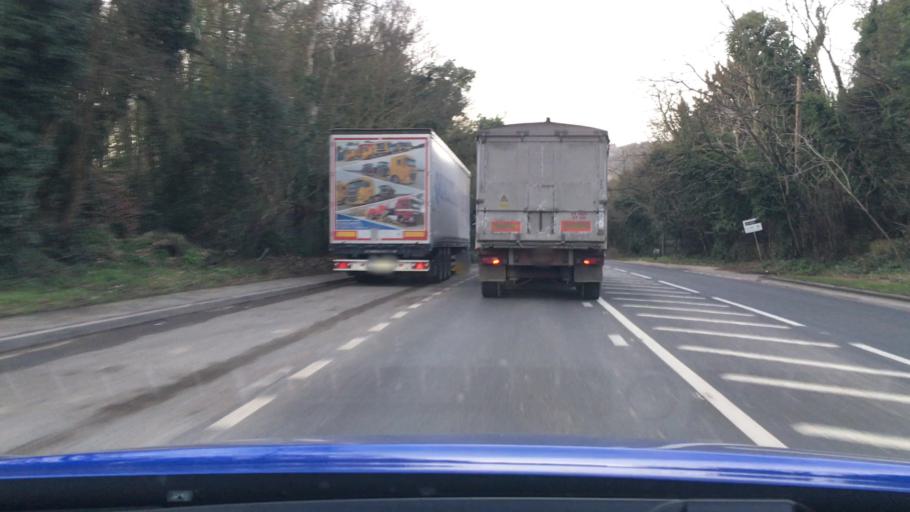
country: GB
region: England
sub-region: Kent
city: Borough Green
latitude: 51.2990
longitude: 0.3389
